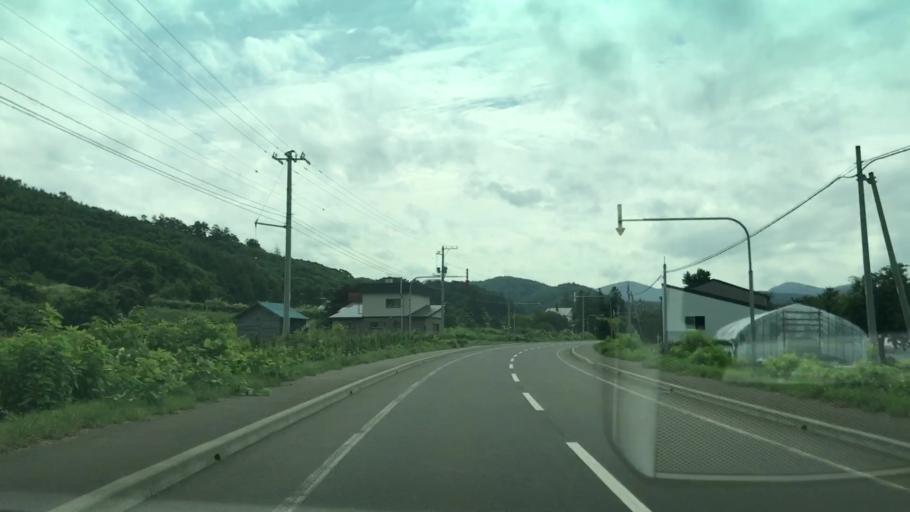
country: JP
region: Hokkaido
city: Yoichi
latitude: 43.1839
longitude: 140.8440
